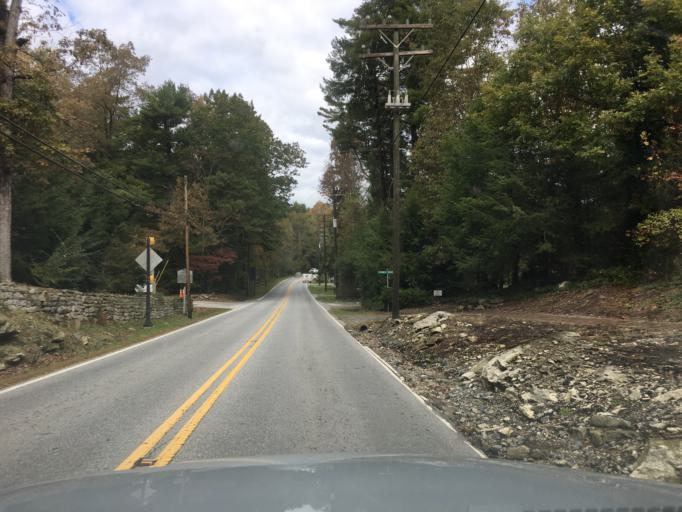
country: US
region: North Carolina
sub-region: Henderson County
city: Flat Rock
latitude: 35.2738
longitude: -82.4423
